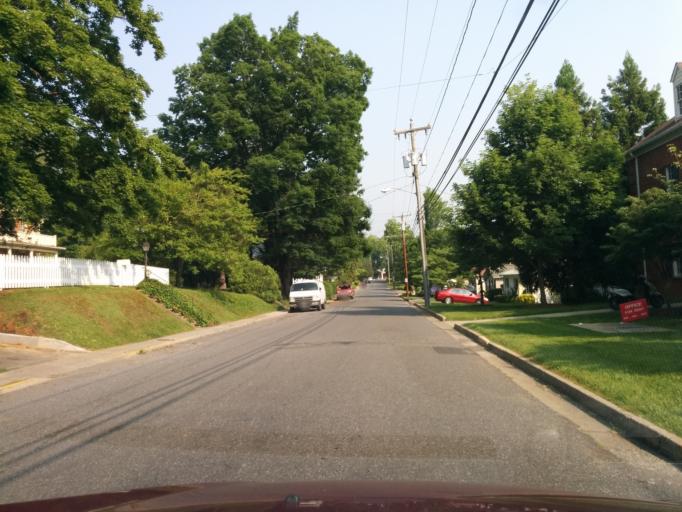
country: US
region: Virginia
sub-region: City of Lexington
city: Lexington
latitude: 37.7776
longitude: -79.4442
